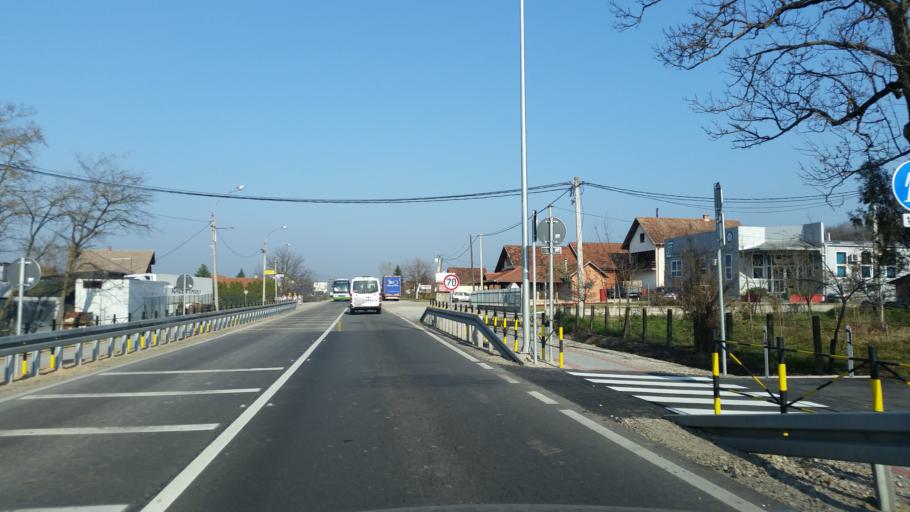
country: RS
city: Prislonica
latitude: 43.9195
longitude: 20.4083
